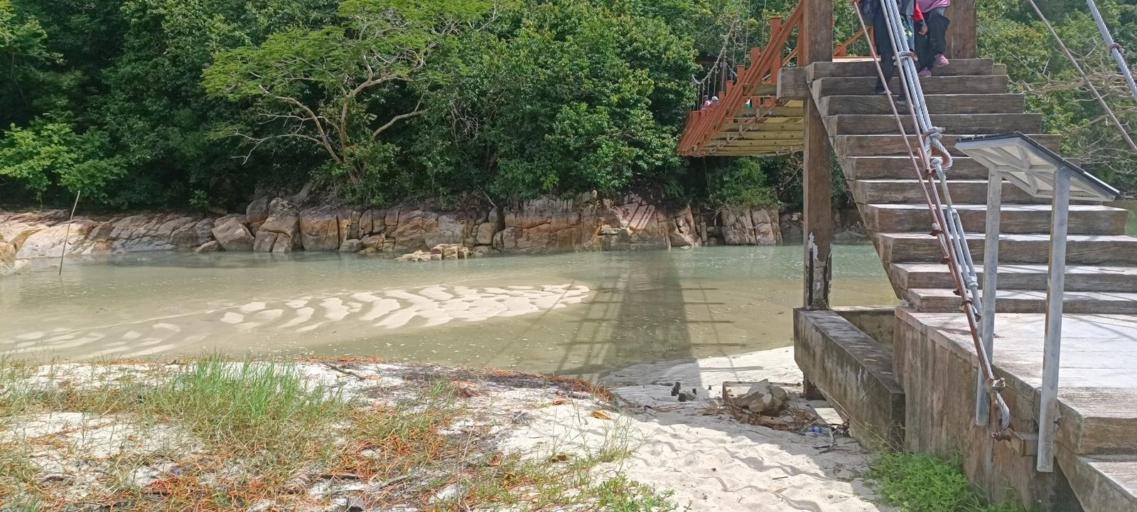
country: MY
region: Penang
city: Tanjung Tokong
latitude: 5.4530
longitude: 100.1843
